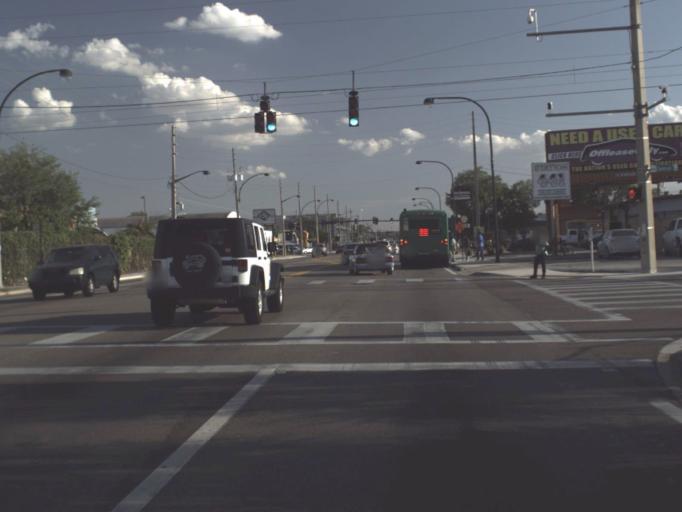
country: US
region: Florida
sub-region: Orange County
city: Orlando
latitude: 28.5422
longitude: -81.3974
